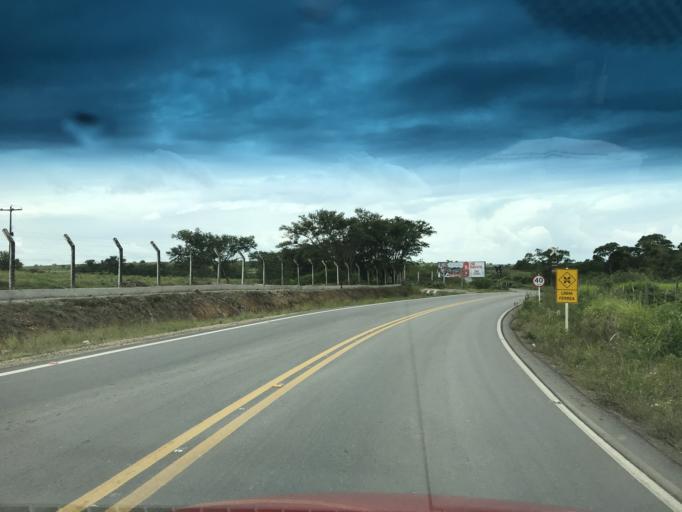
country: BR
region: Bahia
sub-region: Castro Alves
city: Castro Alves
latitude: -12.7573
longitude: -39.4164
